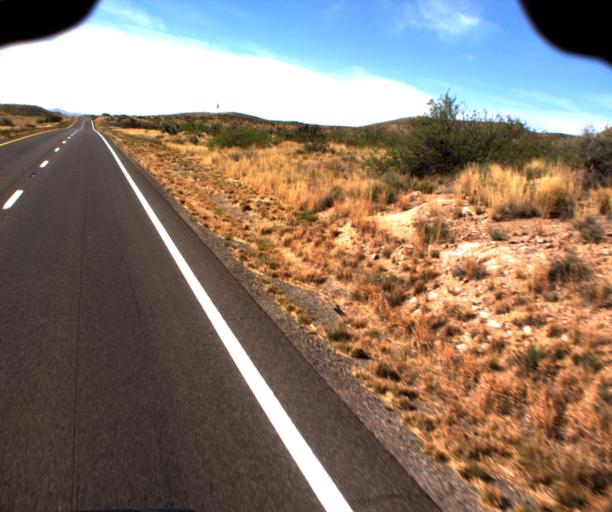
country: US
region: Arizona
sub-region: Graham County
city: Swift Trail Junction
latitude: 32.5203
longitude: -109.6741
